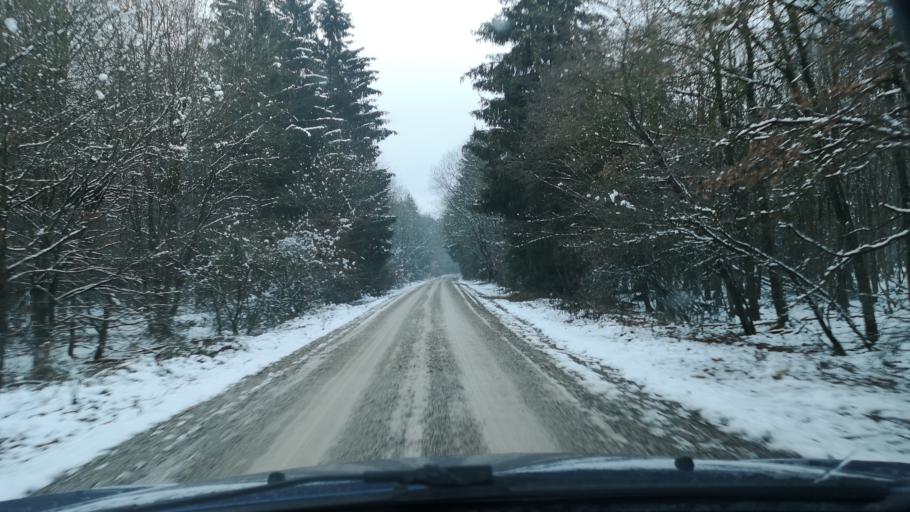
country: DE
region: Bavaria
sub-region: Upper Bavaria
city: Anzing
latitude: 48.1352
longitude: 11.8746
